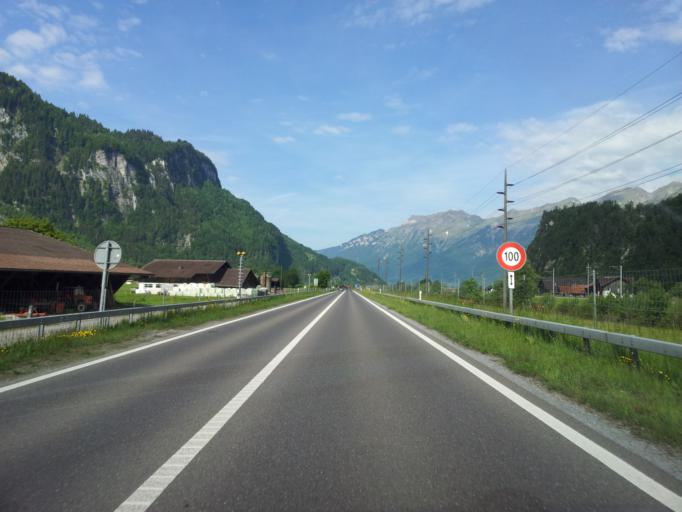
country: CH
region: Bern
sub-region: Interlaken-Oberhasli District
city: Brienz
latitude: 46.7440
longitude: 8.0832
